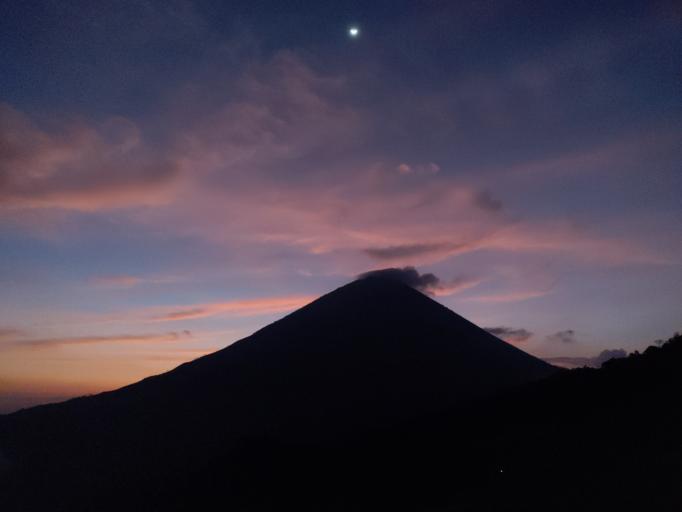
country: ID
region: East Nusa Tenggara
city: Nuamuzi
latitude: -8.8644
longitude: 120.9946
